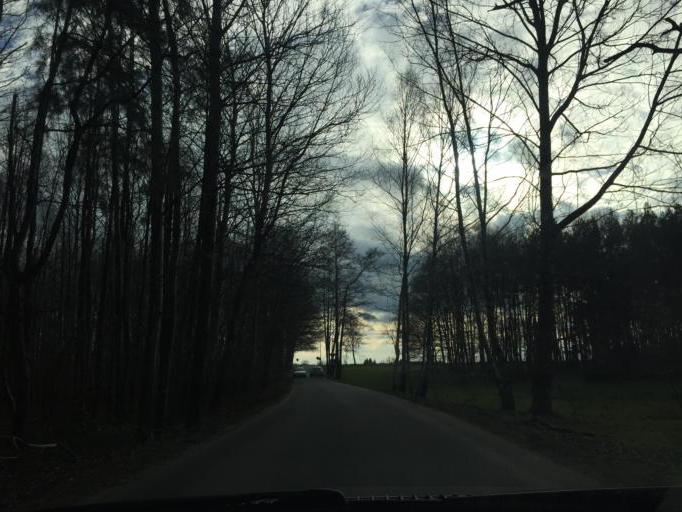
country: DE
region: Saxony
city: Ebersbach
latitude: 51.2090
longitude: 13.6723
